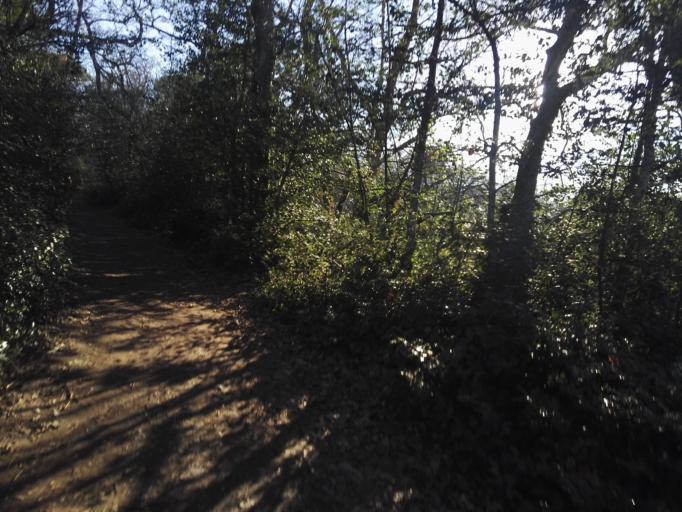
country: FR
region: Aquitaine
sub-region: Departement de la Gironde
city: Pessac
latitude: 44.8209
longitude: -0.6442
